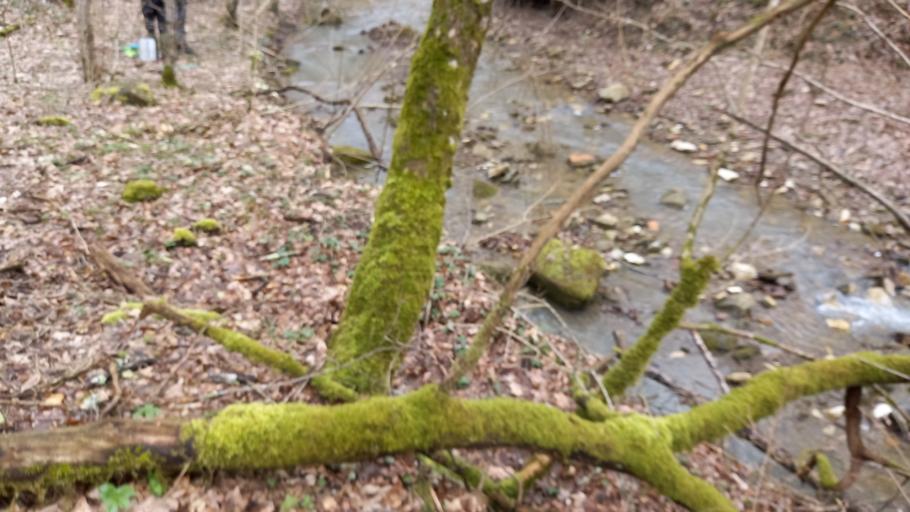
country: RU
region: Krasnodarskiy
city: Pshada
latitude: 44.4933
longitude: 38.3870
